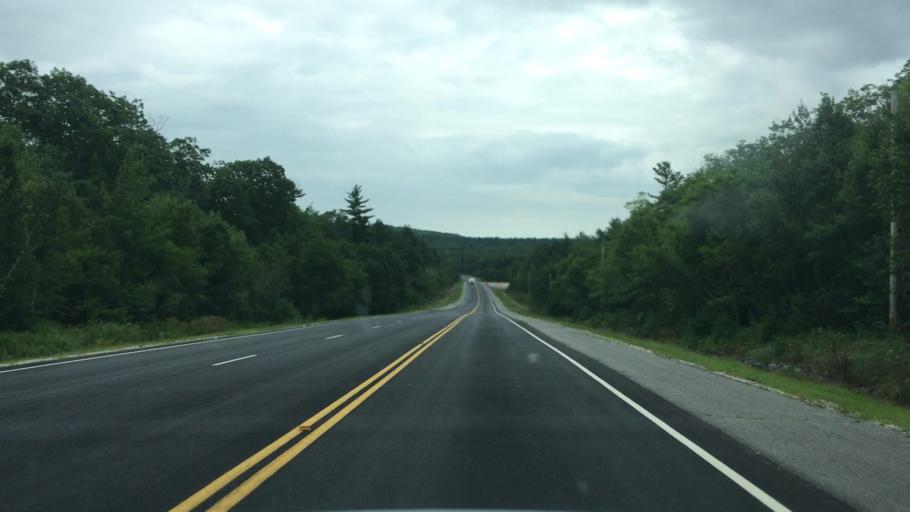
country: US
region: Maine
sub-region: Washington County
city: Cherryfield
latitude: 44.8780
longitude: -67.8754
